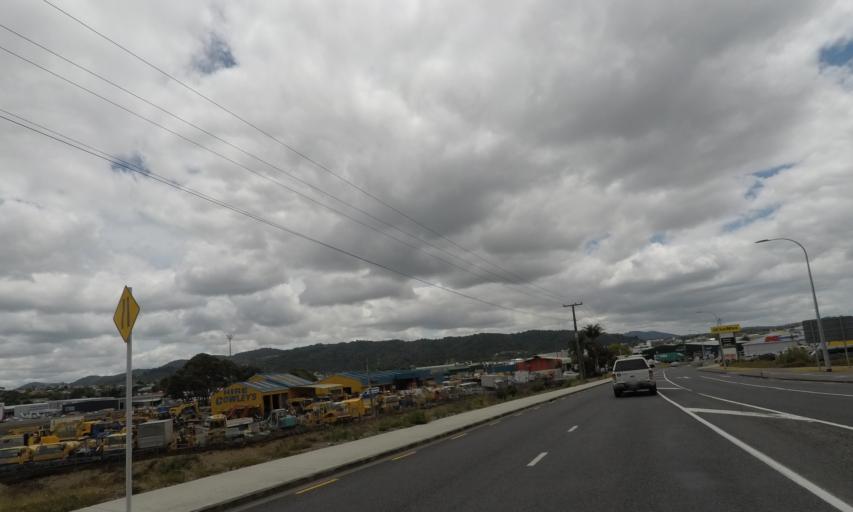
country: NZ
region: Northland
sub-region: Whangarei
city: Whangarei
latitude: -35.7329
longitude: 174.3271
